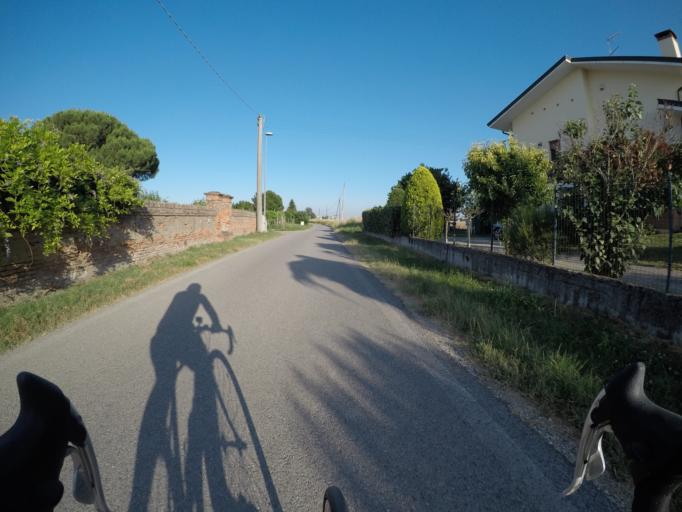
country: IT
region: Veneto
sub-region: Provincia di Rovigo
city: Fratta Polesine
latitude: 45.0294
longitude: 11.6527
